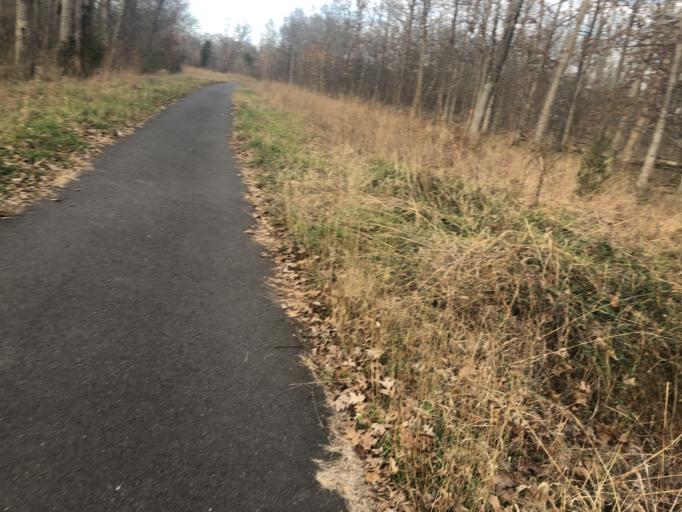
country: US
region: Virginia
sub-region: Fairfax County
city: Centreville
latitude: 38.8576
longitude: -77.4777
